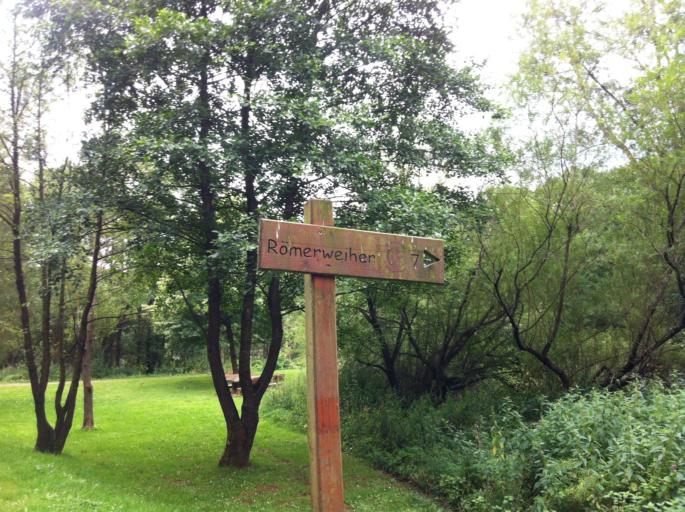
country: DE
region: North Rhine-Westphalia
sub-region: Regierungsbezirk Koln
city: Nettersheim
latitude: 50.4826
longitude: 6.6240
